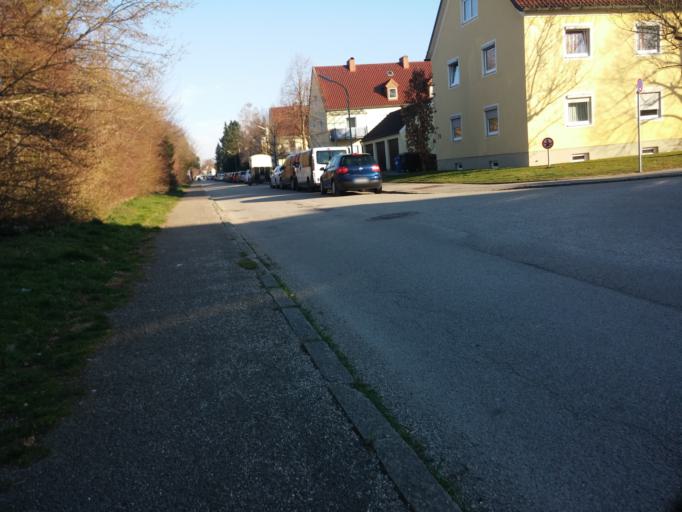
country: DE
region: Bavaria
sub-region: Upper Bavaria
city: Haar
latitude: 48.1166
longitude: 11.6867
